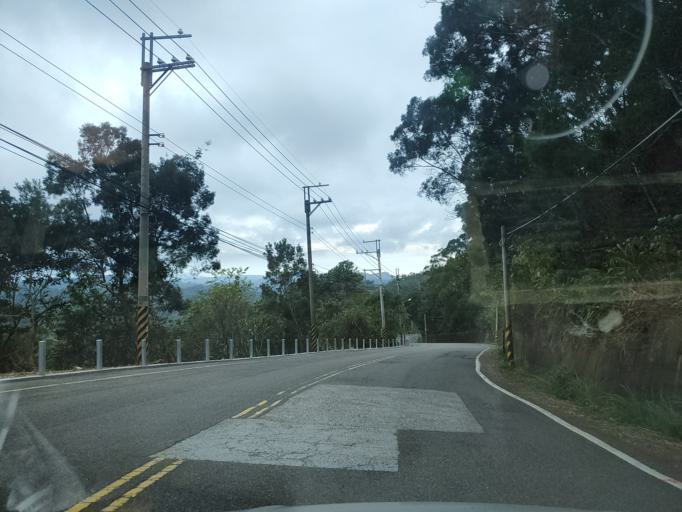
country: TW
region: Taiwan
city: Fengyuan
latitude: 24.3735
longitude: 120.7752
